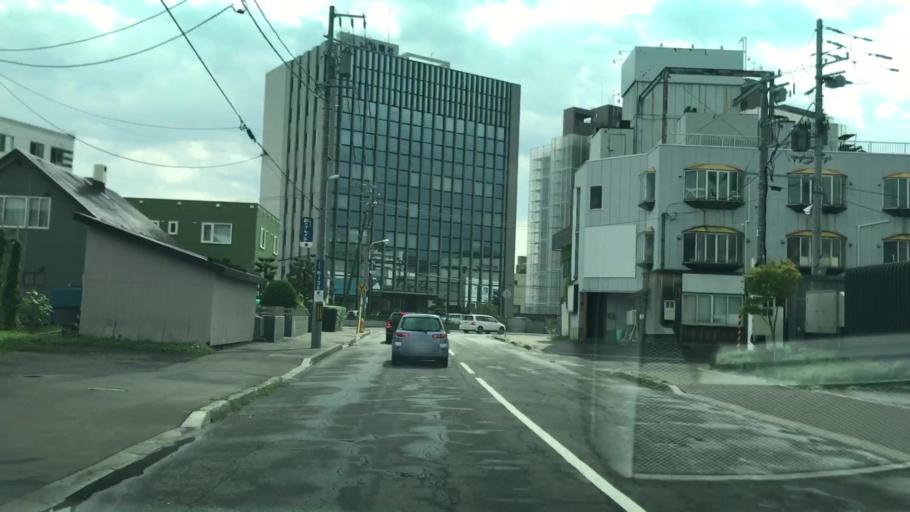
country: JP
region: Hokkaido
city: Sapporo
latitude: 43.0702
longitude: 141.3177
